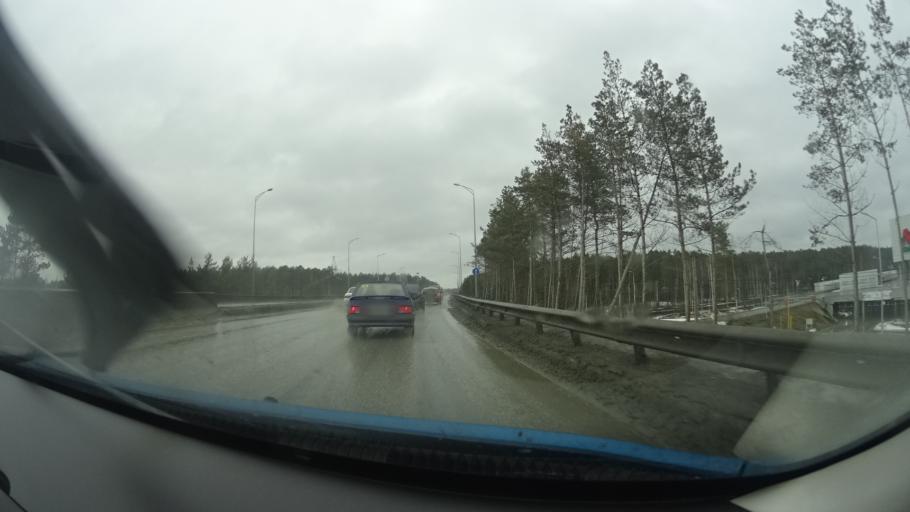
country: RU
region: Perm
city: Perm
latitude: 58.0393
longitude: 56.1884
